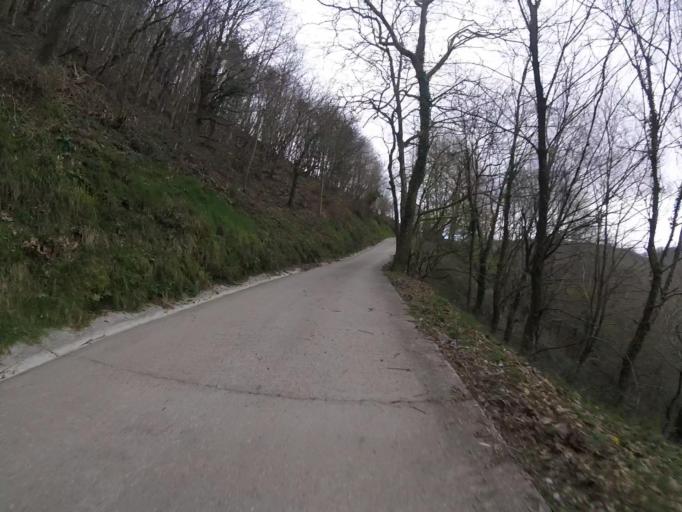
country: ES
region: Basque Country
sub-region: Provincia de Guipuzcoa
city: Errenteria
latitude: 43.2728
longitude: -1.8599
